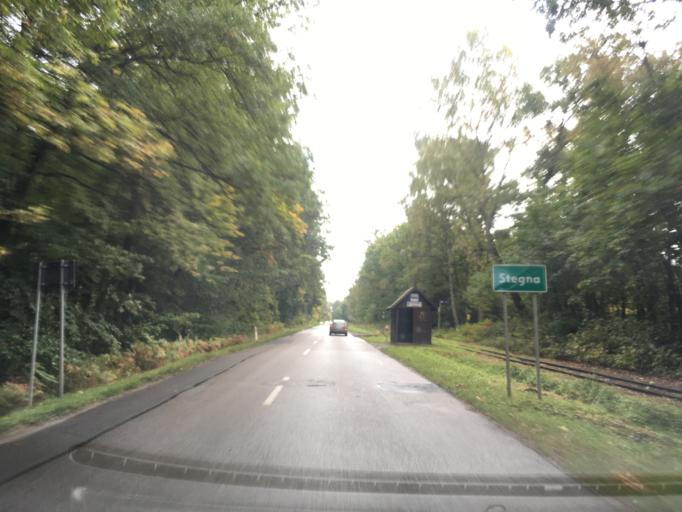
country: PL
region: Pomeranian Voivodeship
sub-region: Powiat nowodworski
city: Stegna
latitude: 54.3317
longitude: 19.0898
